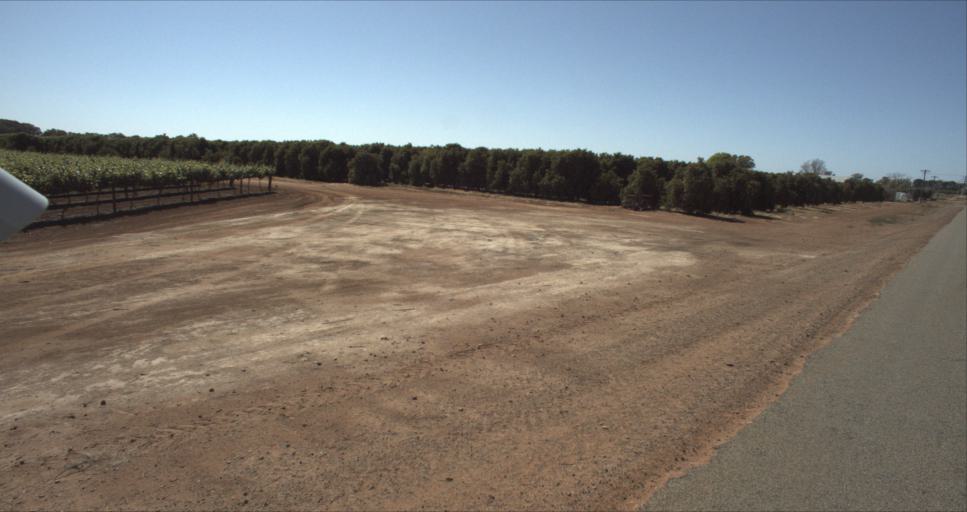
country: AU
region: New South Wales
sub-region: Leeton
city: Leeton
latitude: -34.5357
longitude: 146.3324
